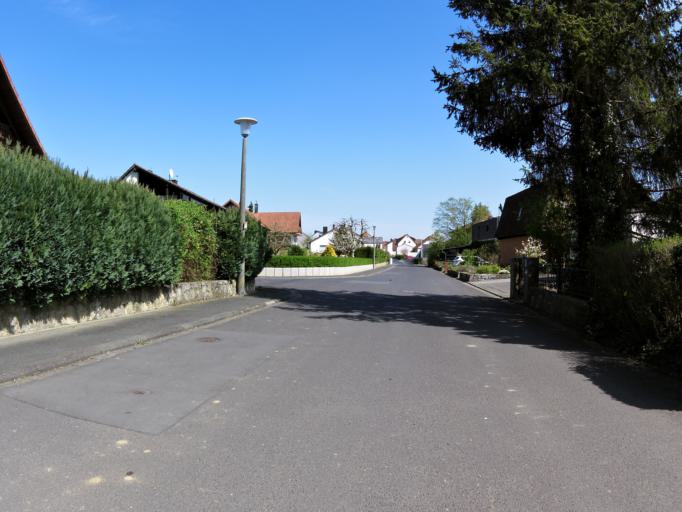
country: DE
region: Bavaria
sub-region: Regierungsbezirk Unterfranken
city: Unterpleichfeld
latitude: 49.8677
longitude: 10.0382
